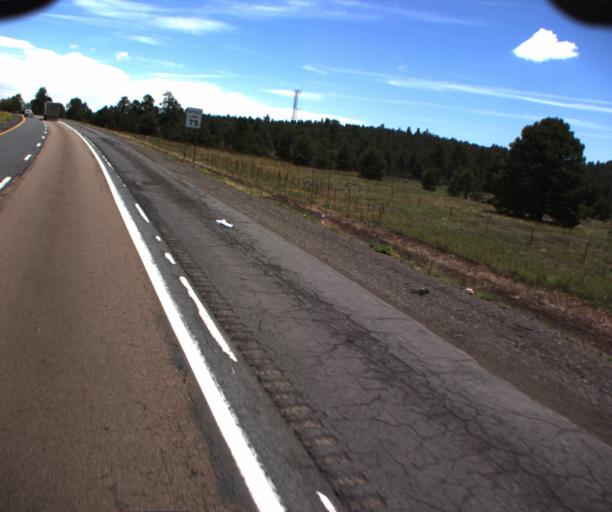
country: US
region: Arizona
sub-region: Coconino County
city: Flagstaff
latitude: 35.1997
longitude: -111.7556
